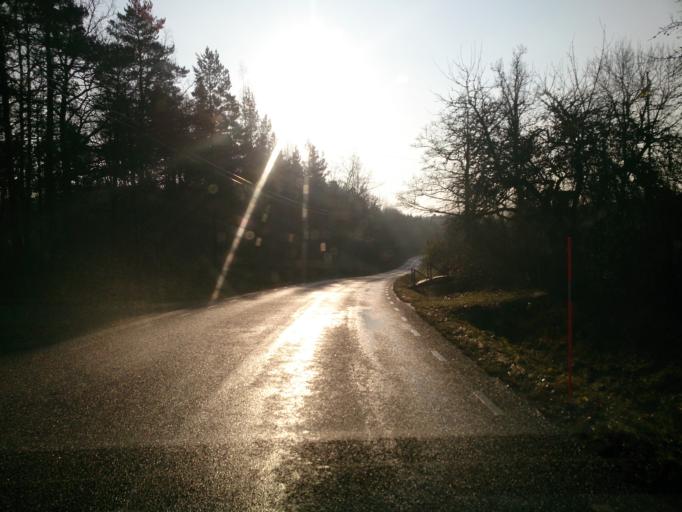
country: SE
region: OEstergoetland
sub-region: Atvidabergs Kommun
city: Atvidaberg
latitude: 58.3190
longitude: 16.0273
